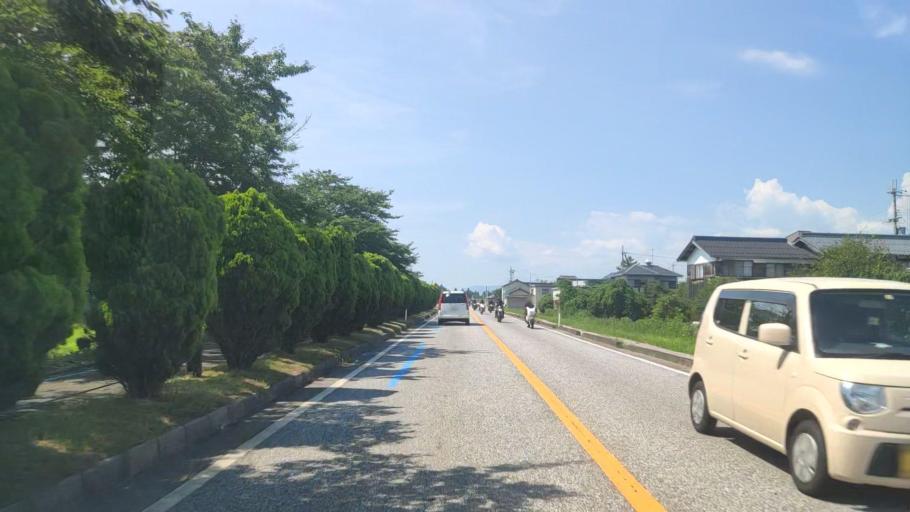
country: JP
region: Shiga Prefecture
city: Nagahama
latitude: 35.4012
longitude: 136.2156
